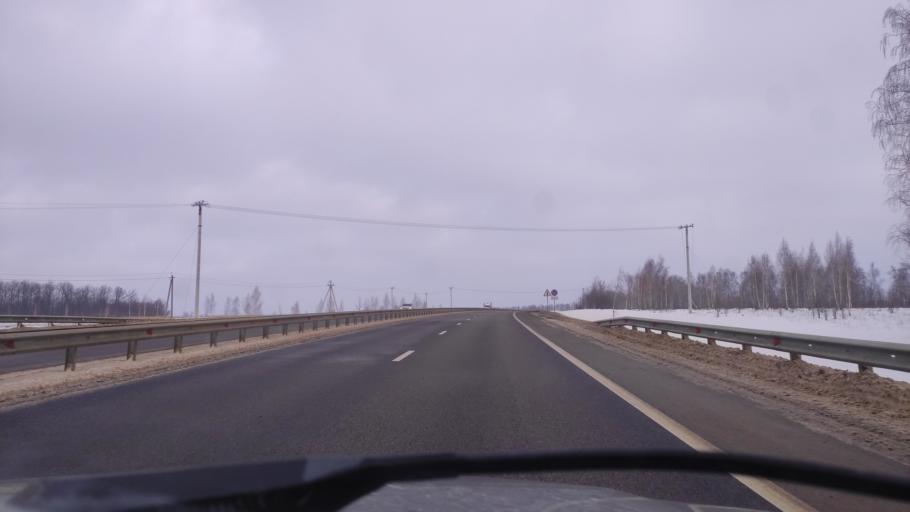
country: RU
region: Tambov
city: Zavoronezhskoye
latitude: 52.9754
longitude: 40.5522
